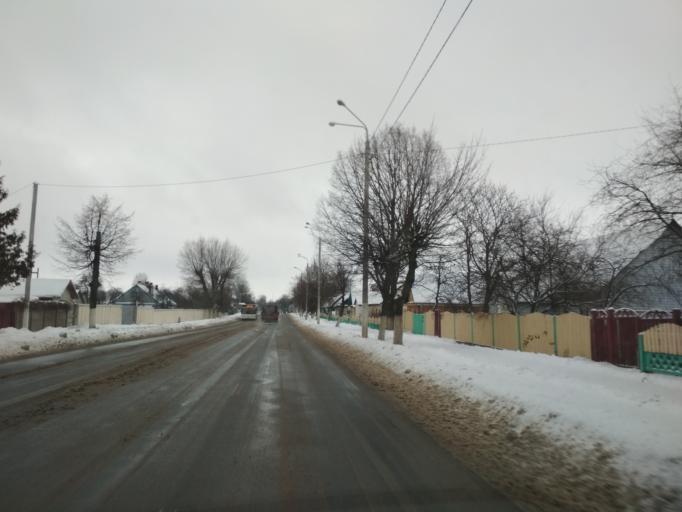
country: BY
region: Minsk
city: Mar''ina Horka
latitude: 53.5075
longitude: 28.1455
